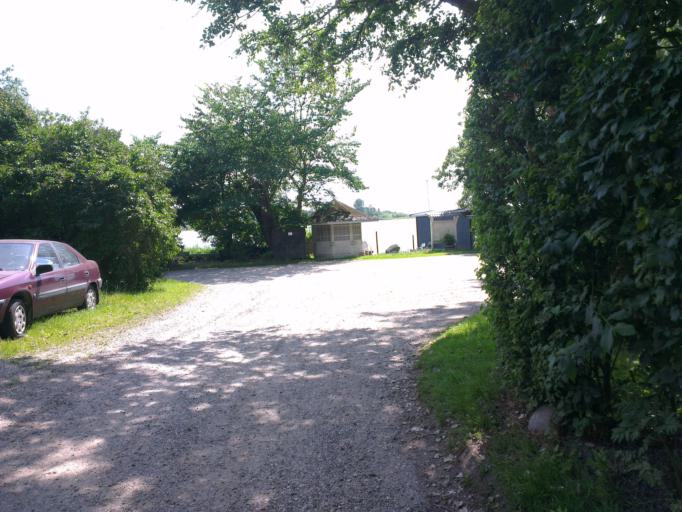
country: DK
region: Zealand
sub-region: Lejre Kommune
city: Ejby
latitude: 55.7373
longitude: 11.8623
